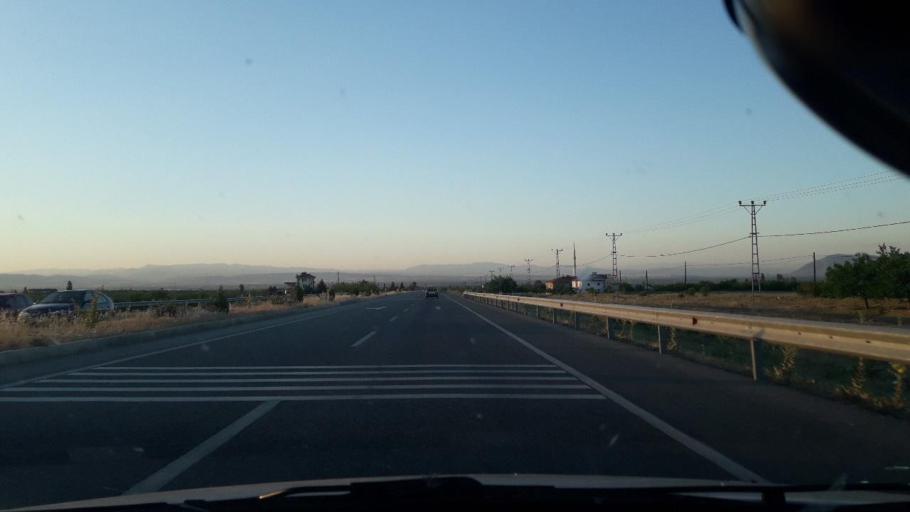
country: TR
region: Malatya
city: Malatya
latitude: 38.4277
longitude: 38.2238
